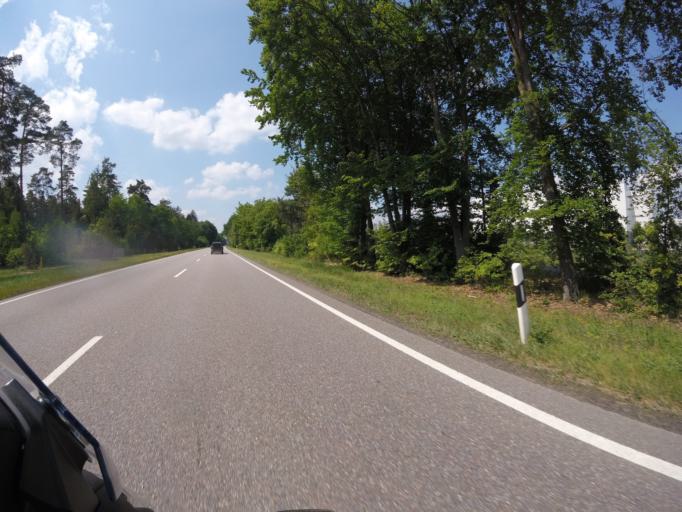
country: DE
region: Bavaria
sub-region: Upper Bavaria
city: Munchsmunster
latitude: 48.7540
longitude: 11.7006
